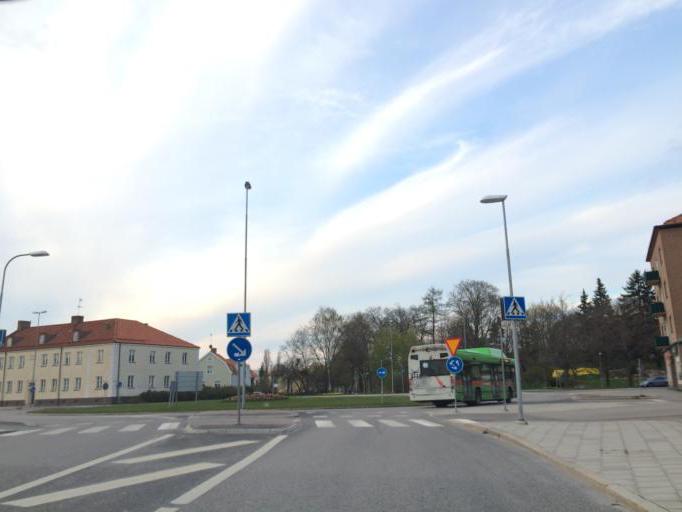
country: SE
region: Soedermanland
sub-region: Eskilstuna Kommun
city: Eskilstuna
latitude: 59.3662
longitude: 16.5258
